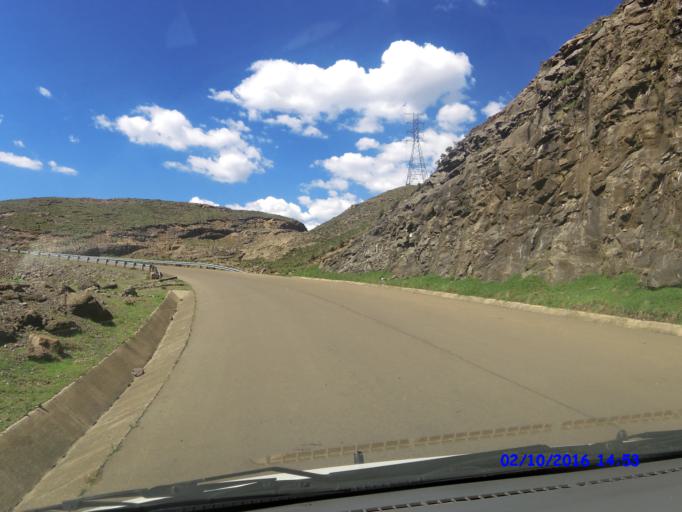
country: LS
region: Maseru
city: Nako
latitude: -29.4769
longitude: 28.0829
